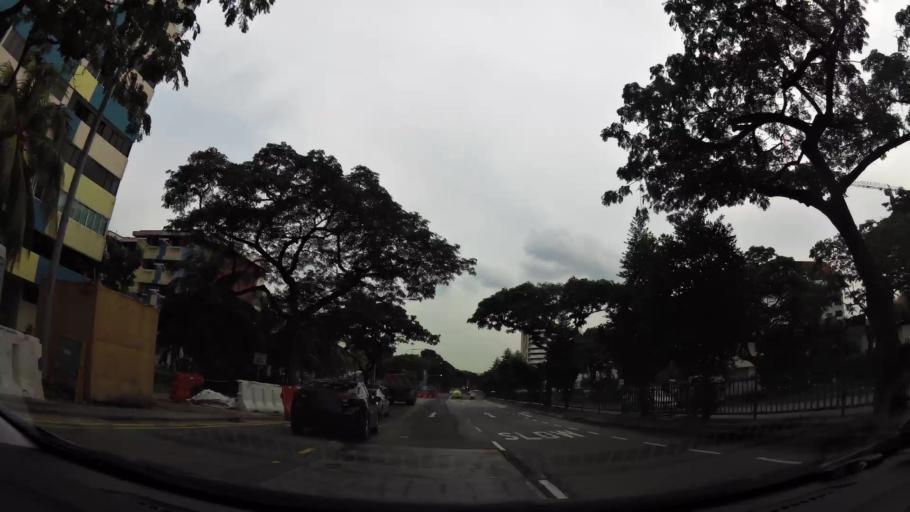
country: SG
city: Singapore
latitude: 1.3627
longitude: 103.8930
